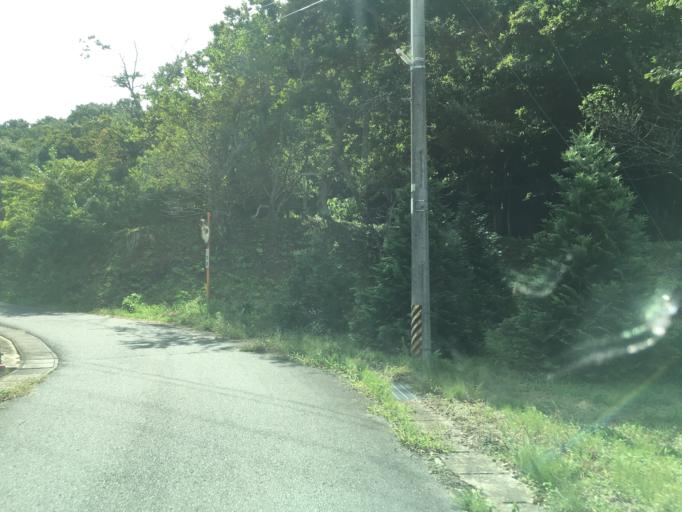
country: JP
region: Fukushima
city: Ishikawa
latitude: 37.2404
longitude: 140.5718
